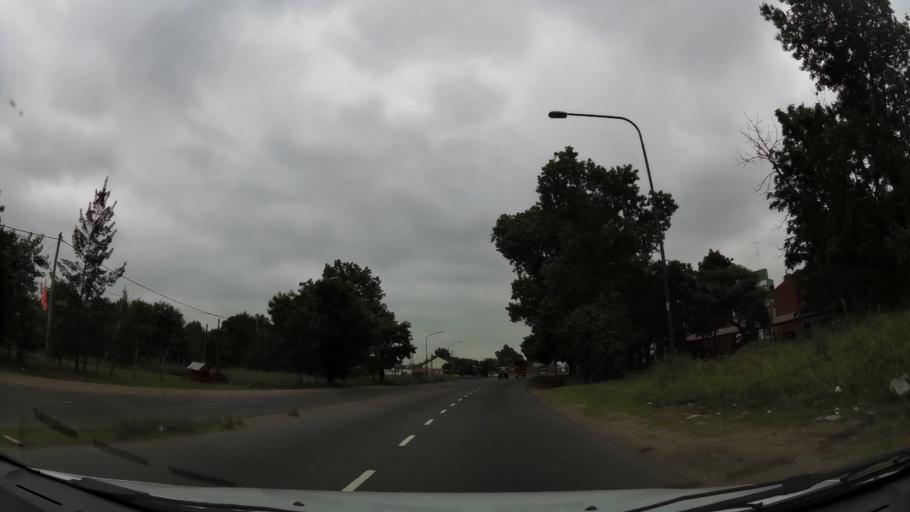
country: AR
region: Buenos Aires
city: San Justo
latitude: -34.7268
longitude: -58.5228
